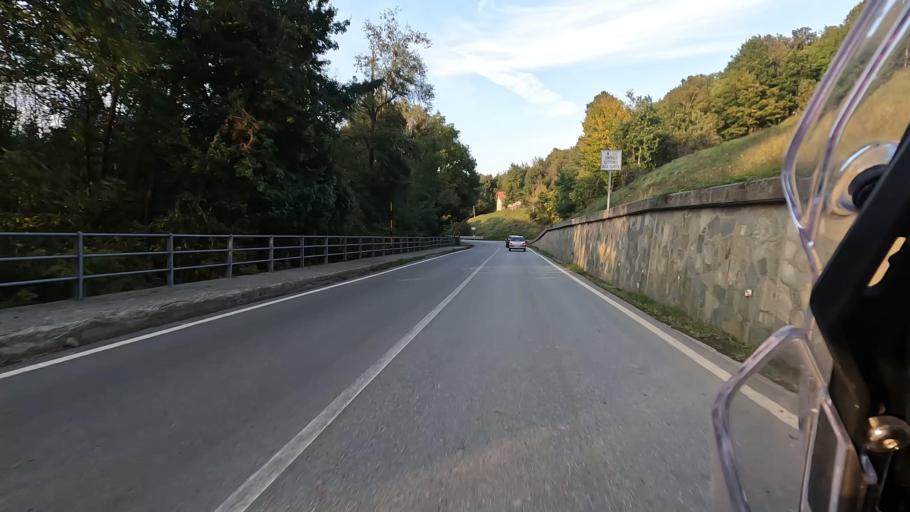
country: IT
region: Liguria
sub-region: Provincia di Savona
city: Sassello
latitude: 44.4673
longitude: 8.4843
